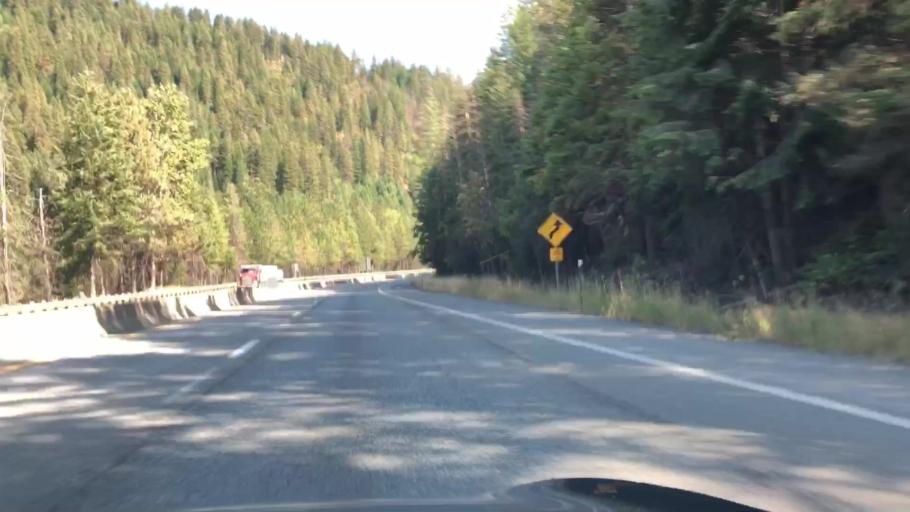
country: US
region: Idaho
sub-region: Shoshone County
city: Wallace
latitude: 47.4735
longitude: -115.8669
